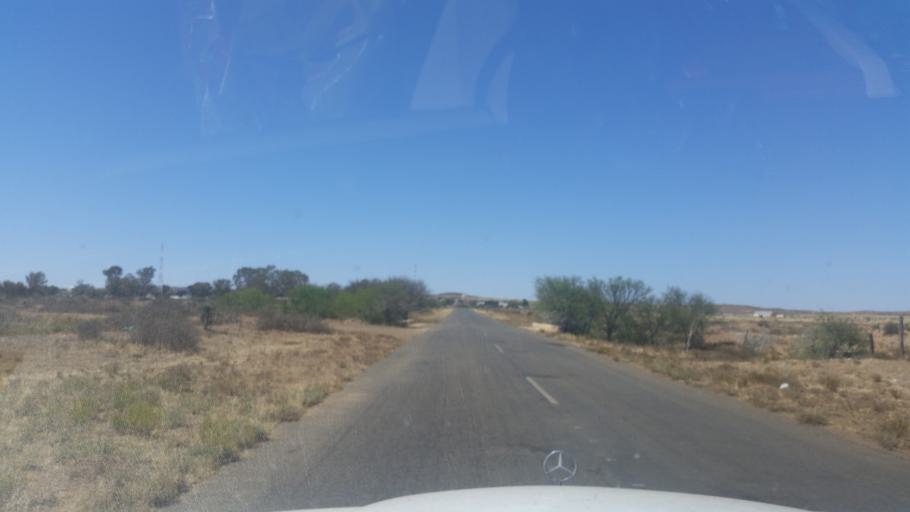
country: ZA
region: Eastern Cape
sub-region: Joe Gqabi District Municipality
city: Burgersdorp
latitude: -30.7701
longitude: 25.7911
